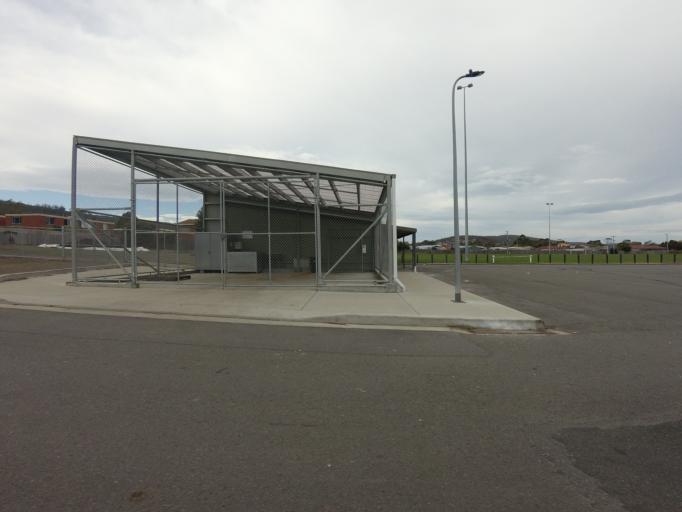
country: AU
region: Tasmania
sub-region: Clarence
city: Howrah
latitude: -42.8783
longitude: 147.3945
